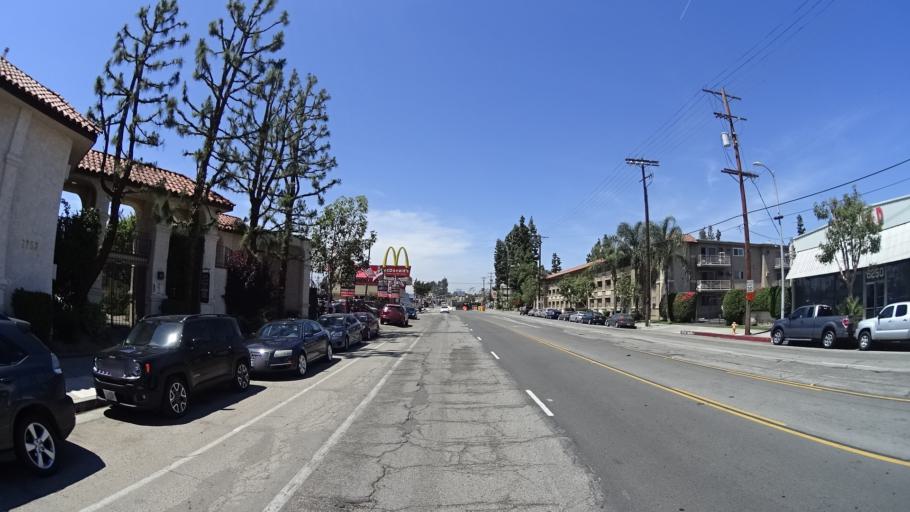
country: US
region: California
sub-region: Los Angeles County
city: North Hollywood
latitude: 34.1844
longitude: -118.3865
